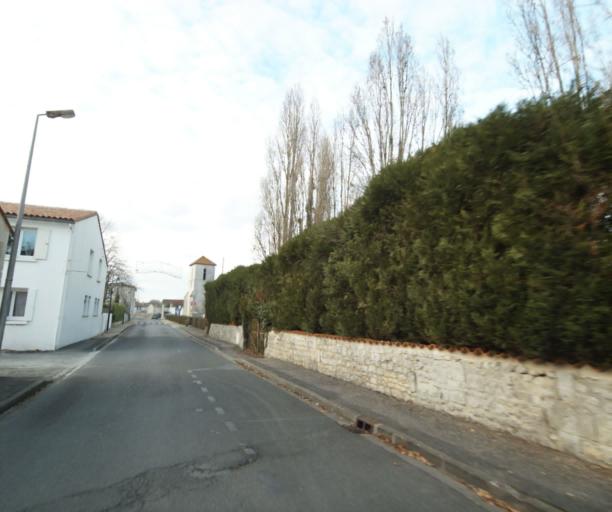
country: FR
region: Poitou-Charentes
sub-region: Departement de la Charente-Maritime
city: Les Gonds
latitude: 45.7147
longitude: -0.6150
